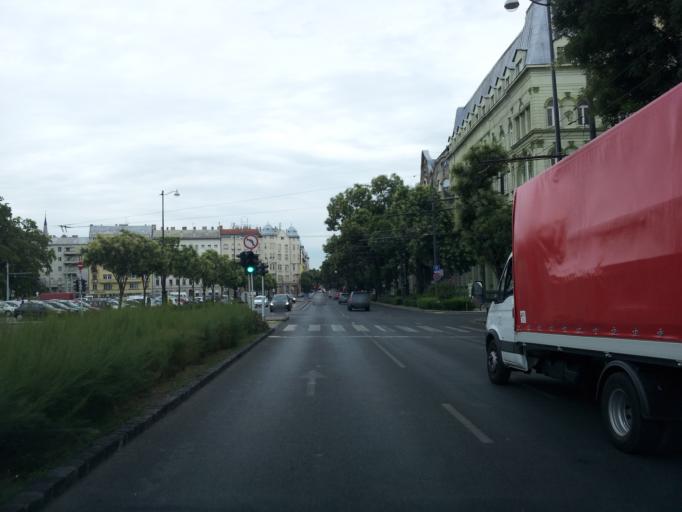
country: HU
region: Budapest
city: Budapest VII. keruelet
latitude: 47.5084
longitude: 19.0838
